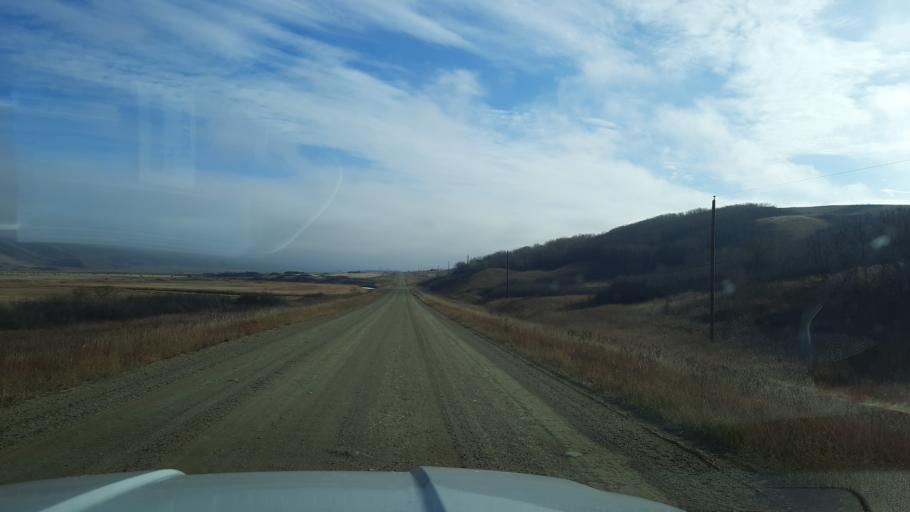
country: CA
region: Saskatchewan
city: Pilot Butte
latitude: 50.7841
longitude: -104.2217
